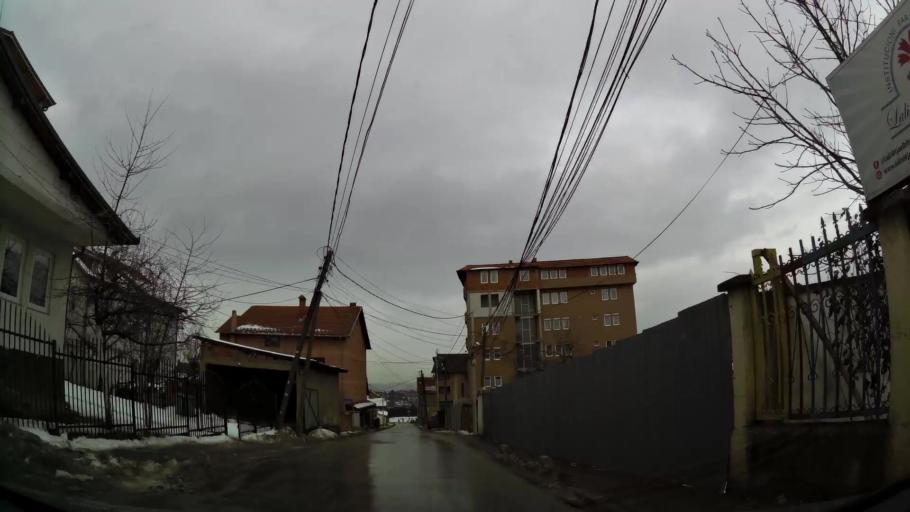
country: XK
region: Pristina
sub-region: Komuna e Prishtines
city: Pristina
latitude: 42.6618
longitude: 21.1815
